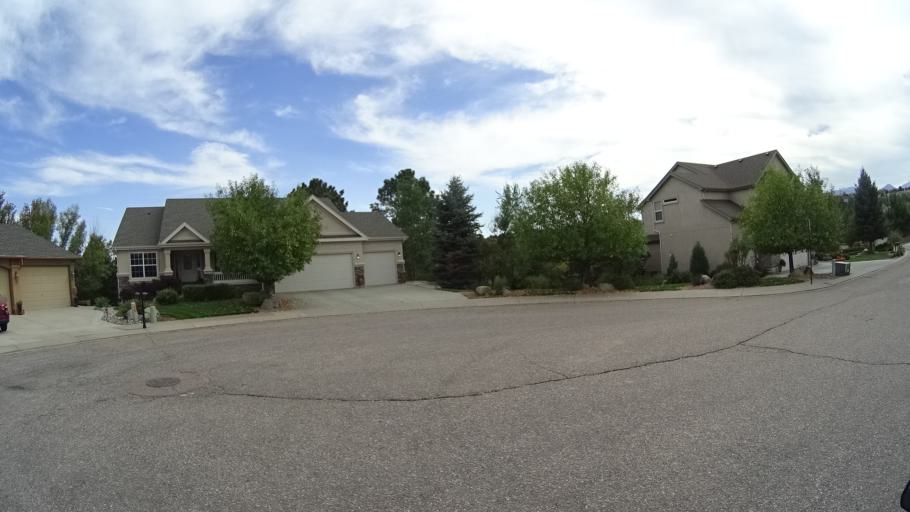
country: US
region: Colorado
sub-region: El Paso County
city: Colorado Springs
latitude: 38.9034
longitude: -104.7854
